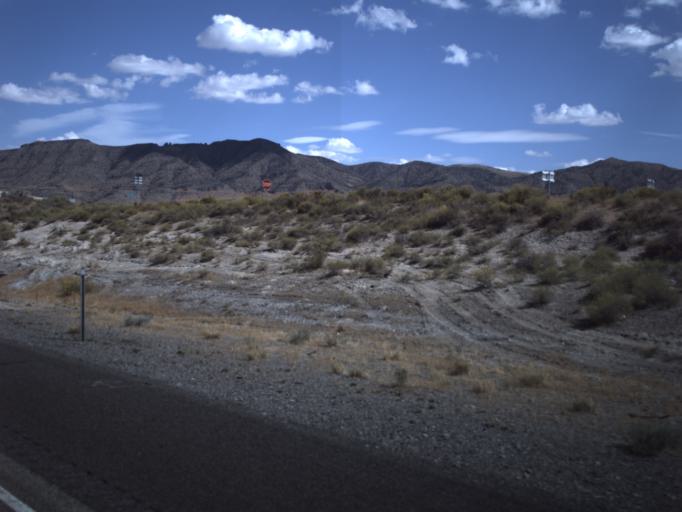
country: US
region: Utah
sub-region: Tooele County
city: Grantsville
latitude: 40.7678
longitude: -112.9853
